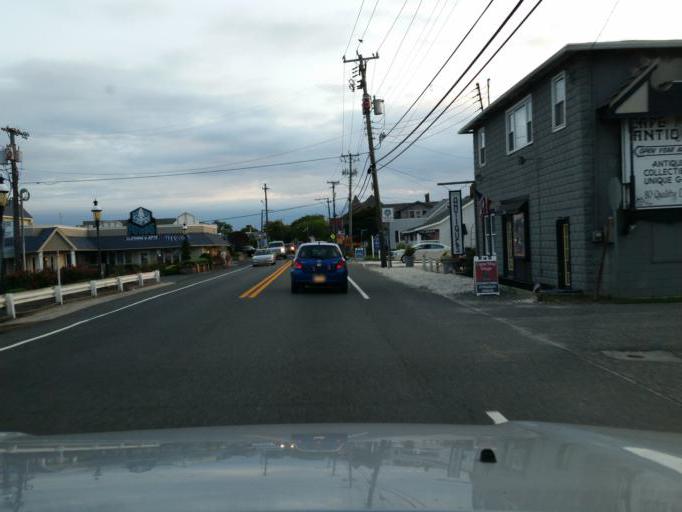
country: US
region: New Jersey
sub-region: Cape May County
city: Cape May
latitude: 38.9495
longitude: -74.9095
